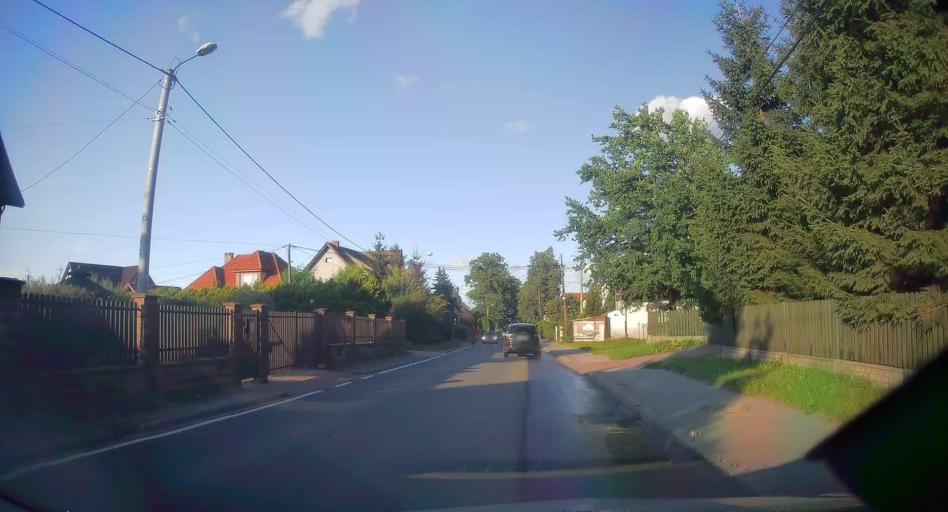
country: PL
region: Lesser Poland Voivodeship
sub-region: Powiat wielicki
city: Kokotow
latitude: 50.0126
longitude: 20.0858
